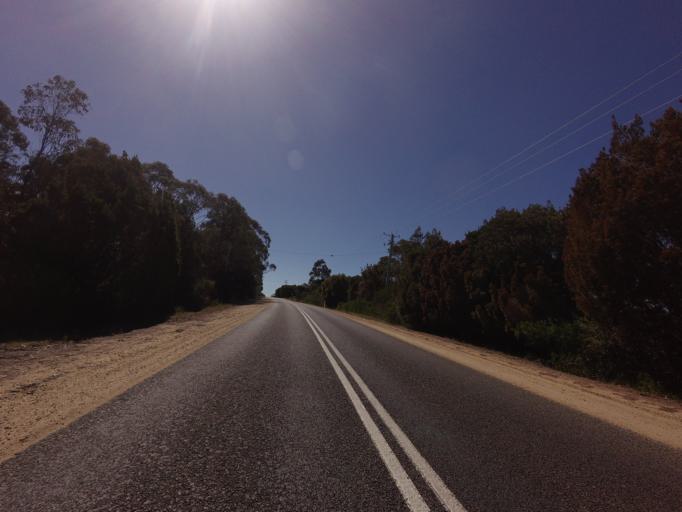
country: AU
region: Tasmania
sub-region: Break O'Day
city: St Helens
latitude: -41.8293
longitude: 148.2605
